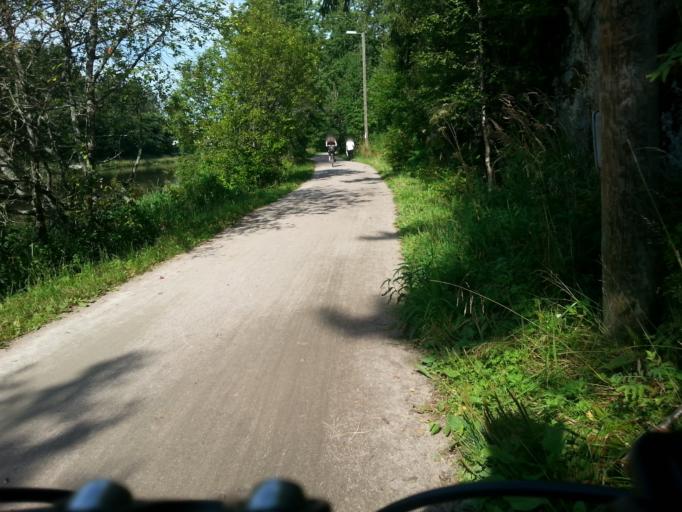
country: FI
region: Uusimaa
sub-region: Helsinki
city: Helsinki
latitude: 60.2288
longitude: 24.9877
